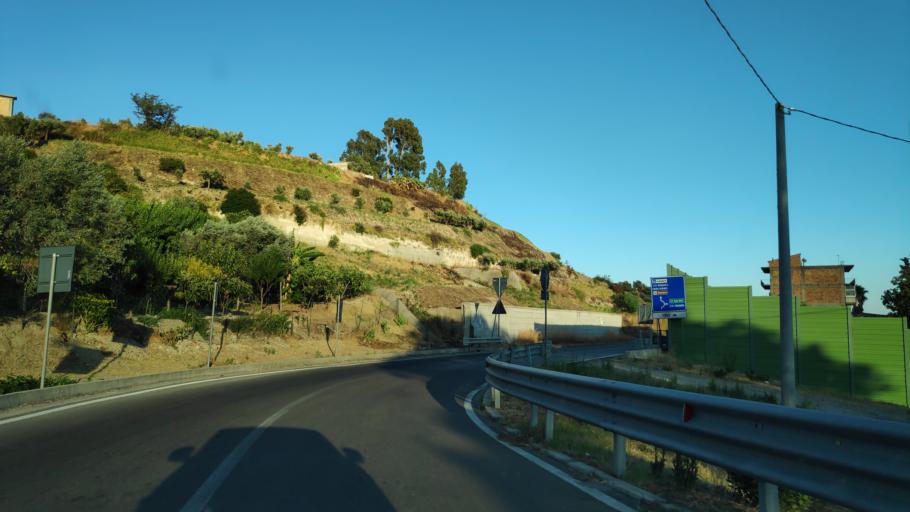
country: IT
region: Calabria
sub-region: Provincia di Reggio Calabria
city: Locri
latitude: 38.2383
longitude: 16.2360
